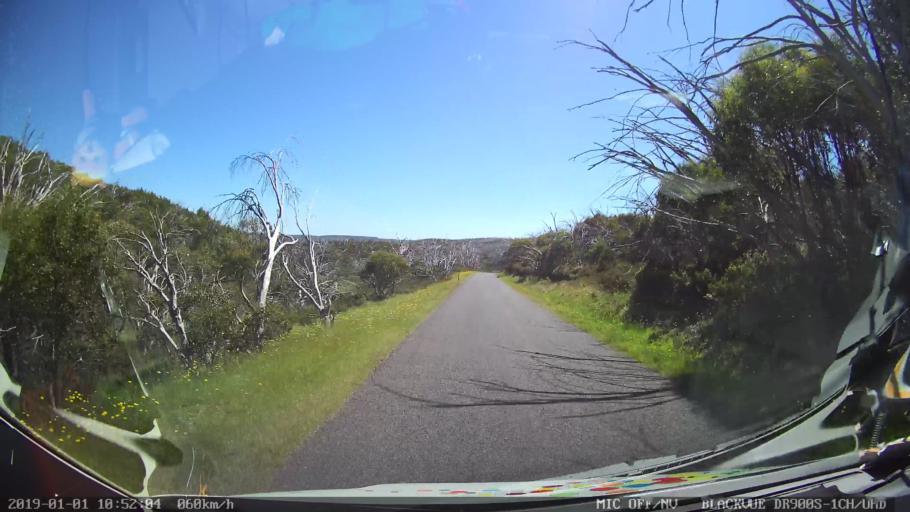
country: AU
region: New South Wales
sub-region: Snowy River
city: Jindabyne
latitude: -36.0180
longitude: 148.3771
